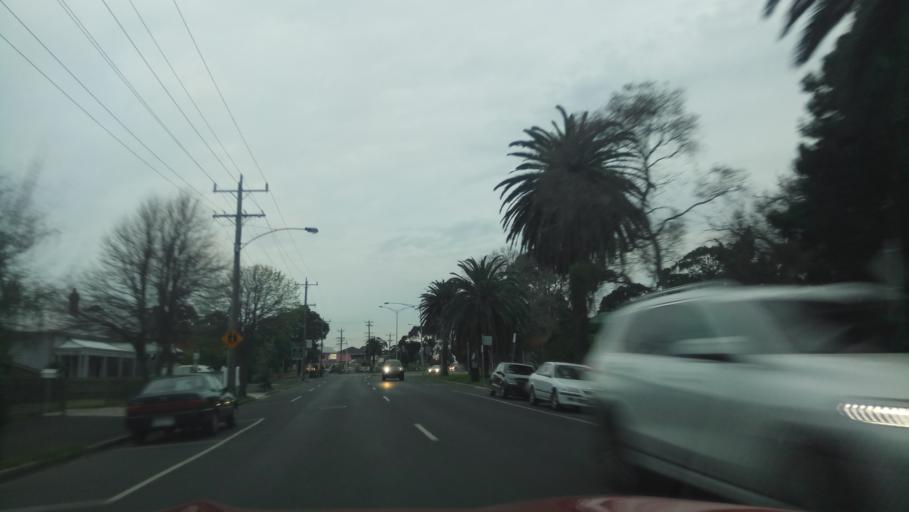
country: AU
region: Victoria
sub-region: Hobsons Bay
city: Williamstown
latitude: -37.8595
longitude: 144.8948
